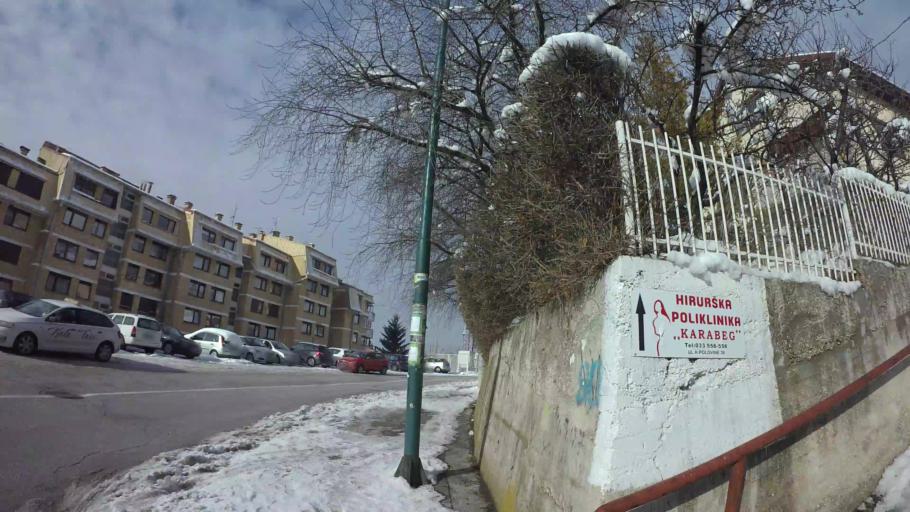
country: BA
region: Federation of Bosnia and Herzegovina
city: Kobilja Glava
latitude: 43.8724
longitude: 18.4194
